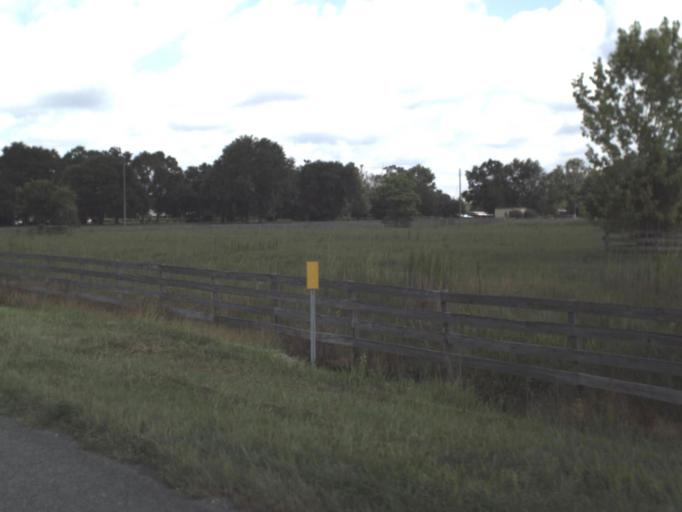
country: US
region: Florida
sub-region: Union County
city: Lake Butler
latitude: 30.0442
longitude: -82.2881
